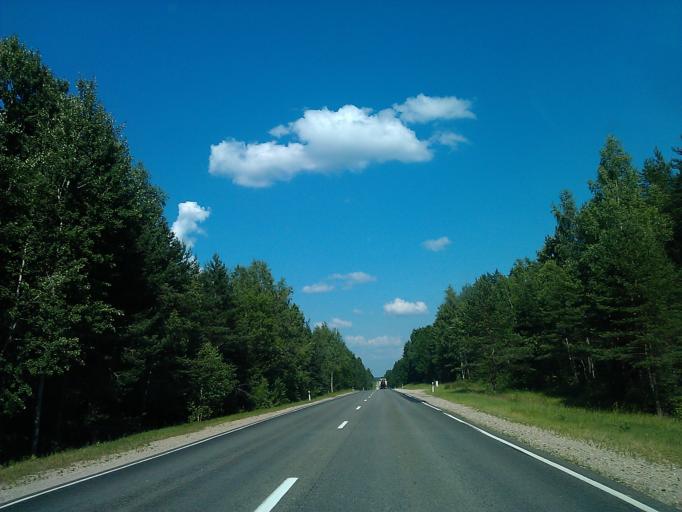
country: LV
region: Skrunda
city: Skrunda
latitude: 56.6548
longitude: 21.9282
